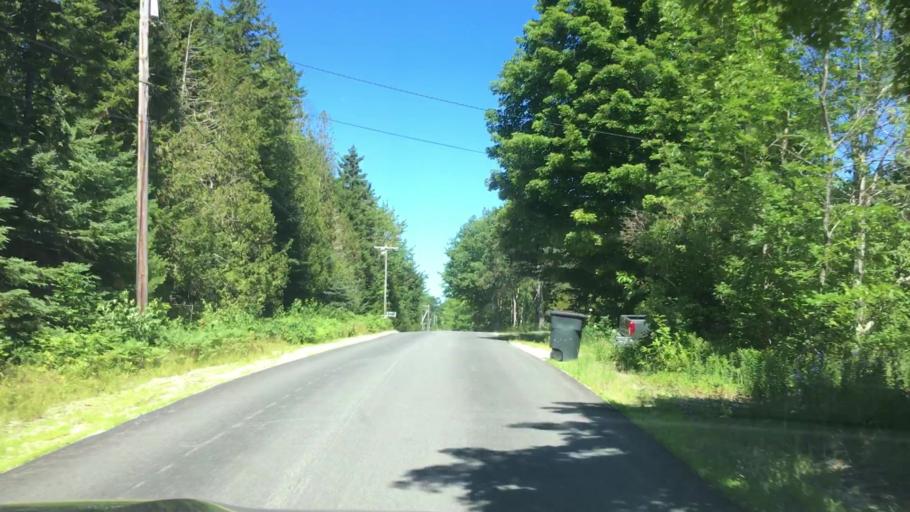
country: US
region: Maine
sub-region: Hancock County
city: Sedgwick
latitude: 44.3187
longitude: -68.6257
